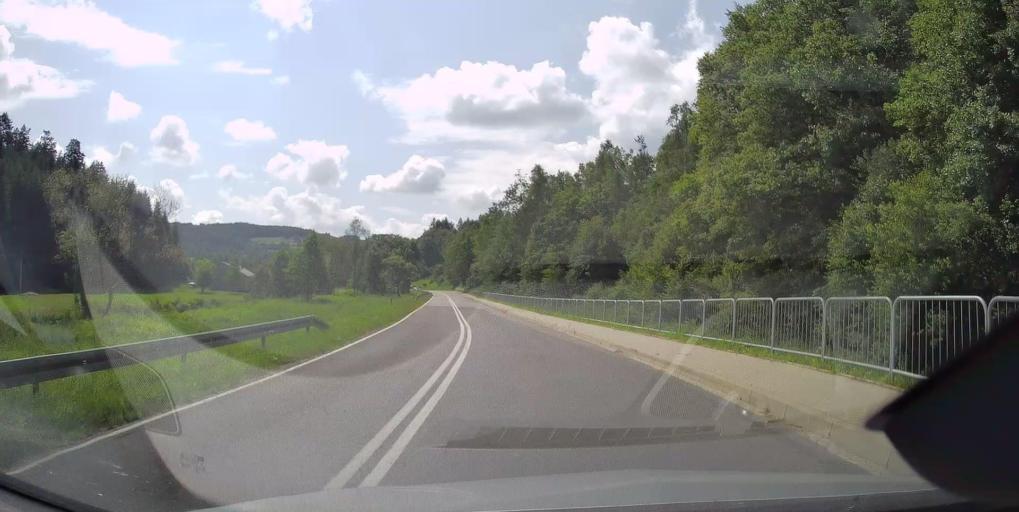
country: PL
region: Lesser Poland Voivodeship
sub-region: Powiat tarnowski
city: Zakliczyn
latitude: 49.8004
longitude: 20.7969
